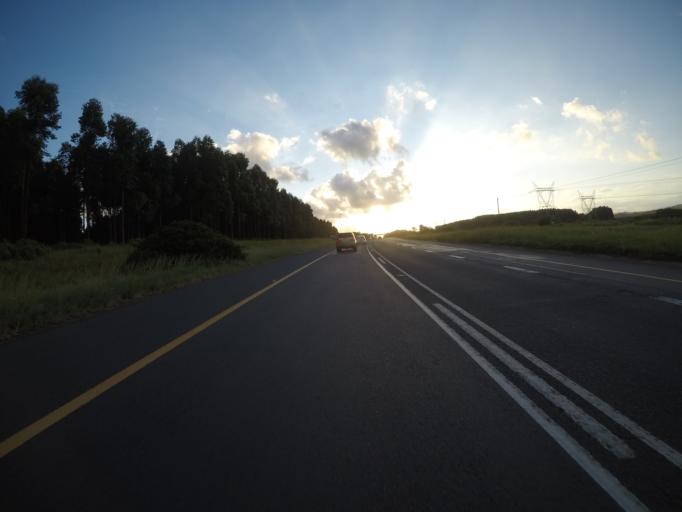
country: ZA
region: KwaZulu-Natal
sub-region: uThungulu District Municipality
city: Richards Bay
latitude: -28.6929
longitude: 32.0344
